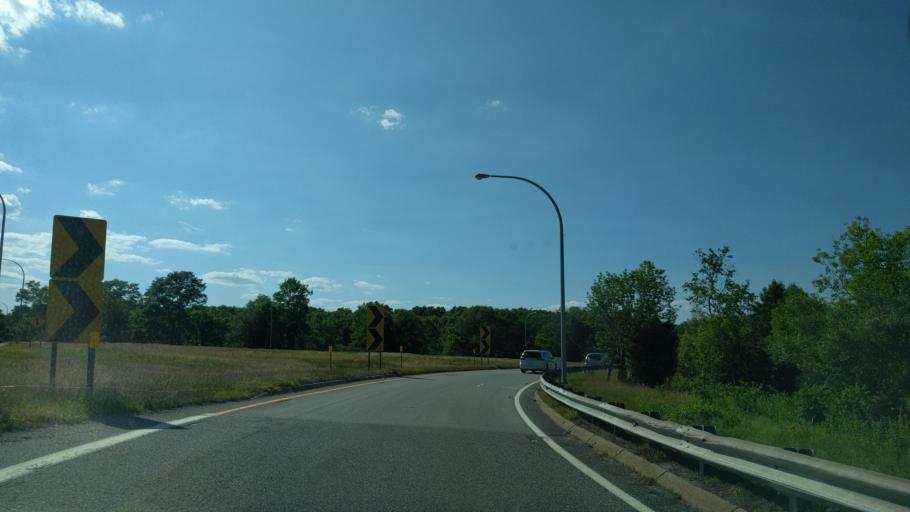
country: US
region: Rhode Island
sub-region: Providence County
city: Cumberland Hill
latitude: 41.9435
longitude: -71.4726
